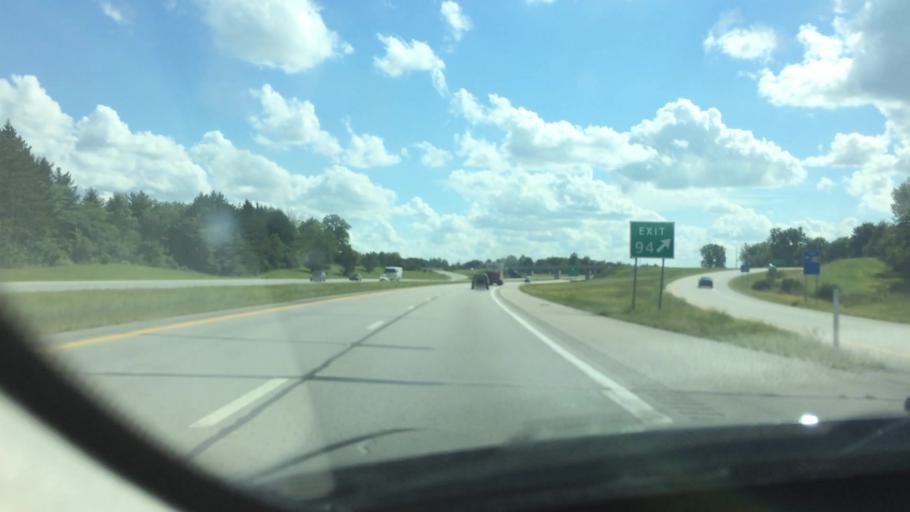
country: US
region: Ohio
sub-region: Shelby County
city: Sidney
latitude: 40.3271
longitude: -84.1602
